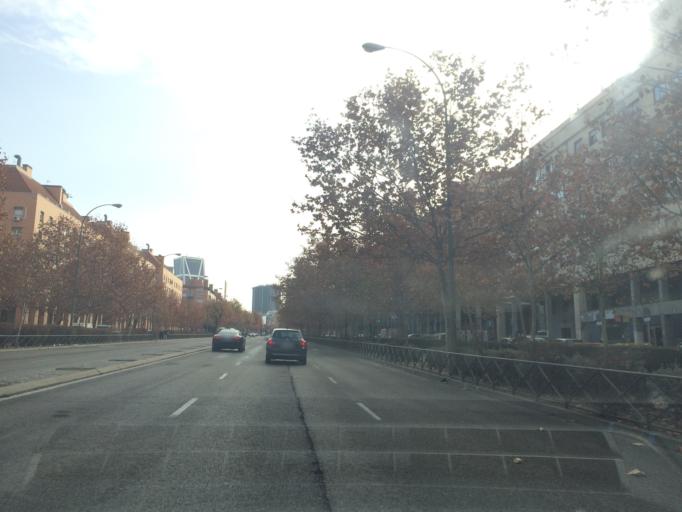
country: ES
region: Madrid
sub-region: Provincia de Madrid
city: Tetuan de las Victorias
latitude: 40.4720
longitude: -3.6992
